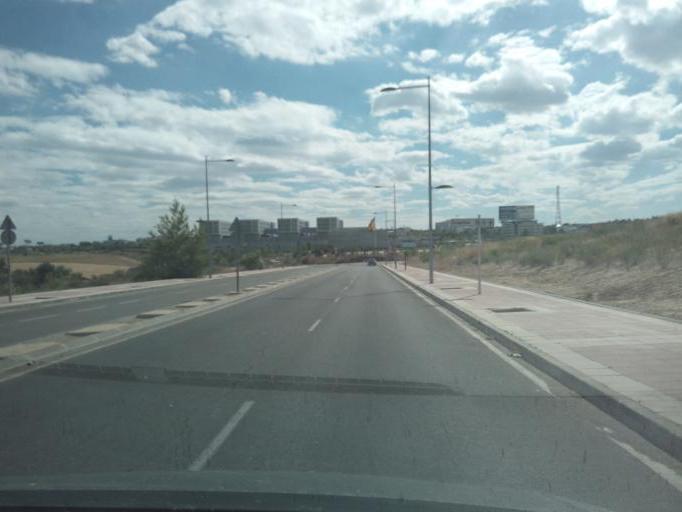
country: ES
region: Madrid
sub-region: Provincia de Madrid
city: San Sebastian de los Reyes
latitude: 40.5627
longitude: -3.6069
